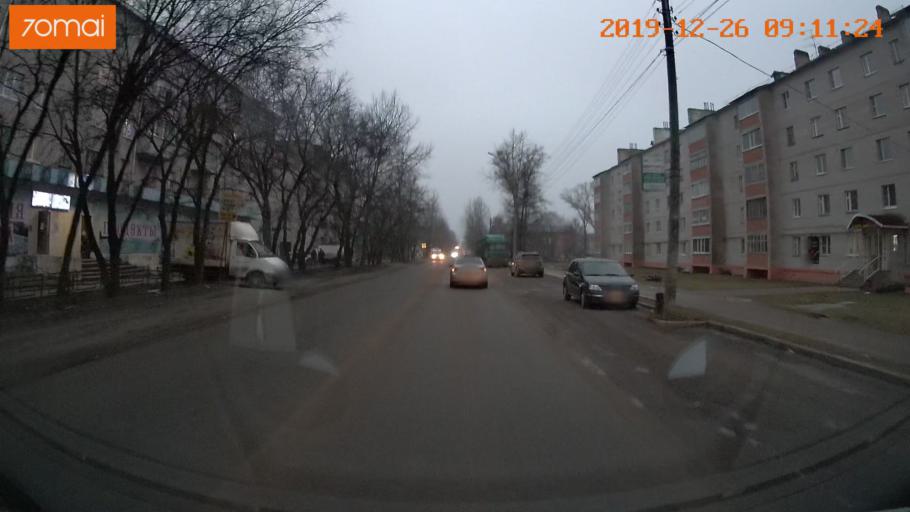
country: RU
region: Vologda
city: Gryazovets
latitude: 58.8759
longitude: 40.2527
